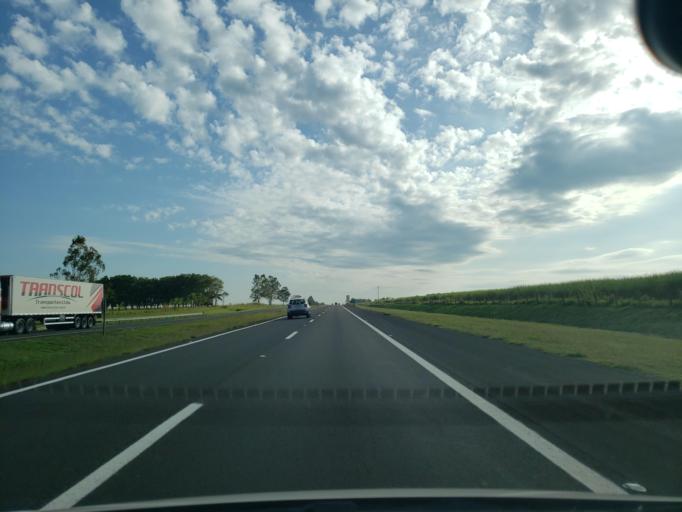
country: BR
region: Sao Paulo
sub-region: Guararapes
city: Guararapes
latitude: -21.2028
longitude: -50.6017
